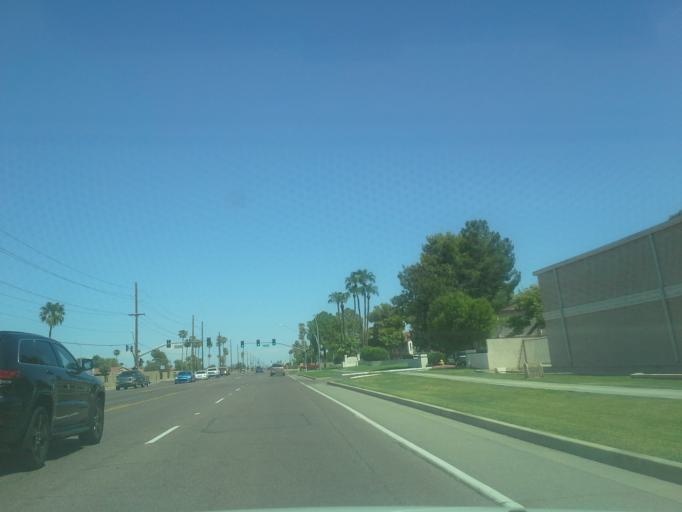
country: US
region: Arizona
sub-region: Maricopa County
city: Litchfield Park
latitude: 33.5368
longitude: -112.3518
